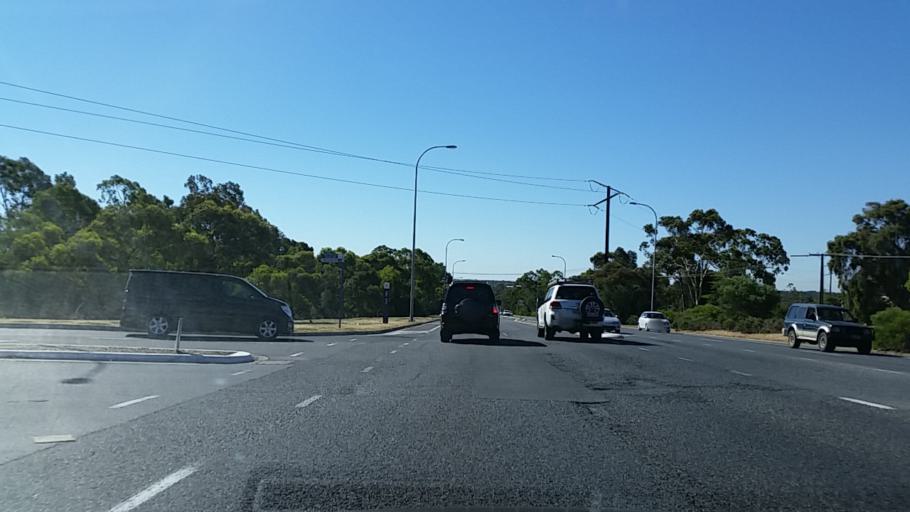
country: AU
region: South Australia
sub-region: Tea Tree Gully
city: Modbury
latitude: -34.8008
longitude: 138.6600
